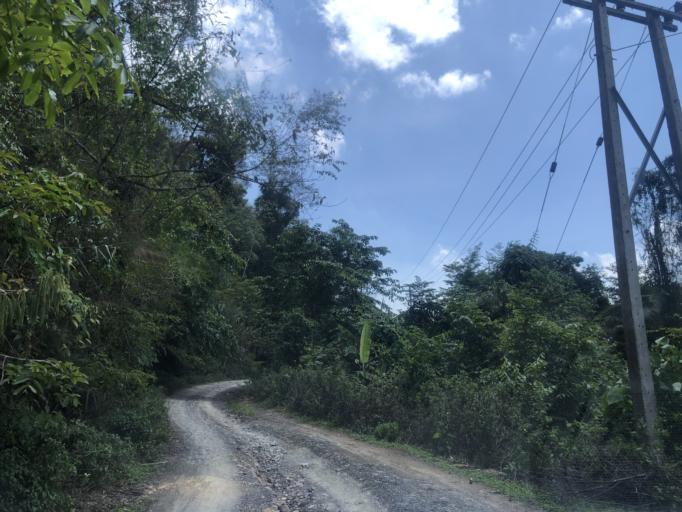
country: LA
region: Phongsali
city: Phongsali
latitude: 21.4475
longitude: 102.1637
